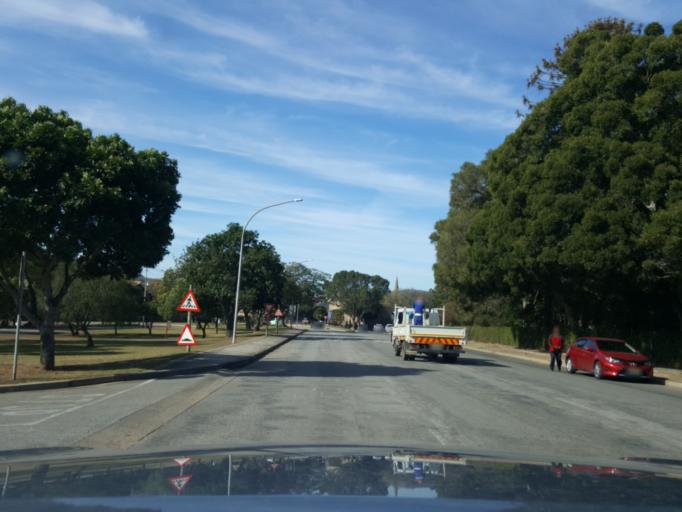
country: ZA
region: Eastern Cape
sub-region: Cacadu District Municipality
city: Grahamstown
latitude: -33.3071
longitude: 26.5163
